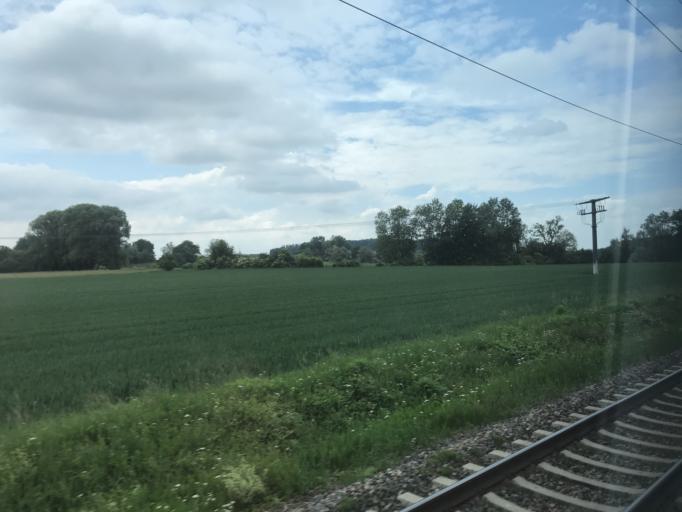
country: DE
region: Bavaria
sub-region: Swabia
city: Nersingen
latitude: 48.4262
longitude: 10.1079
